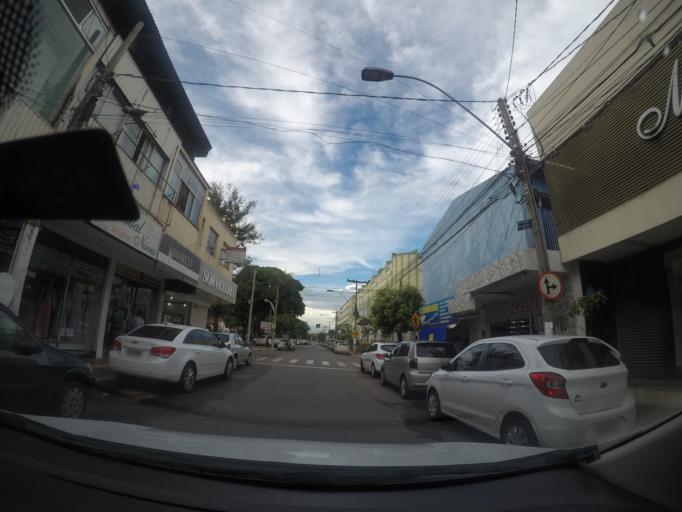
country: BR
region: Goias
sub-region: Goiania
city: Goiania
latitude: -16.6671
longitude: -49.2937
